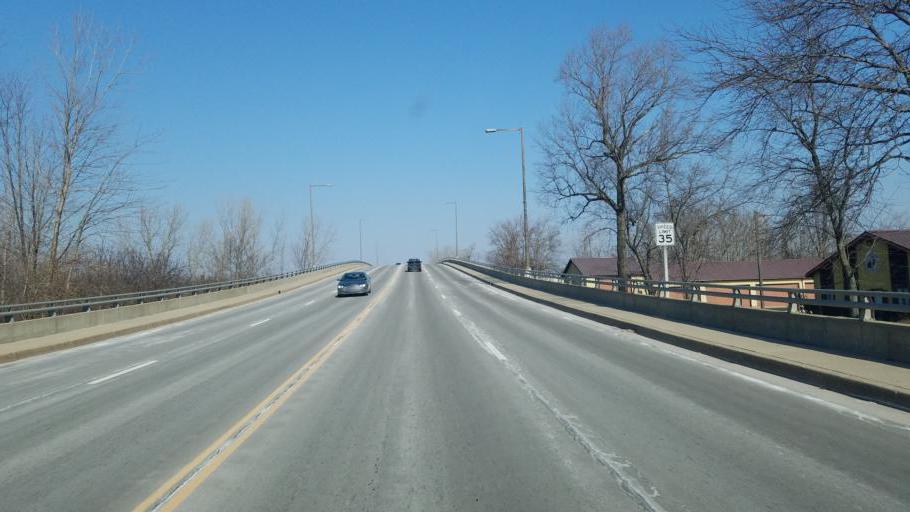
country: US
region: Ohio
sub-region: Crawford County
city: Crestline
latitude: 40.7801
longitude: -82.7382
